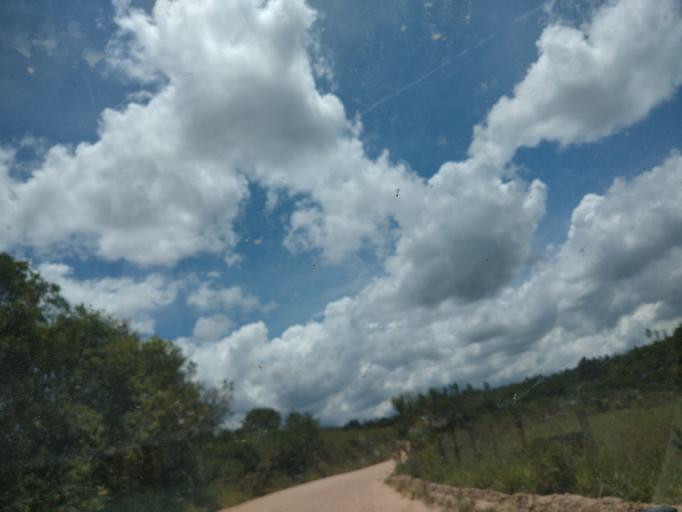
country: BR
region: Minas Gerais
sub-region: Sao Joao Del Rei
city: Sao Joao del Rei
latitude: -20.9000
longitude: -44.3010
